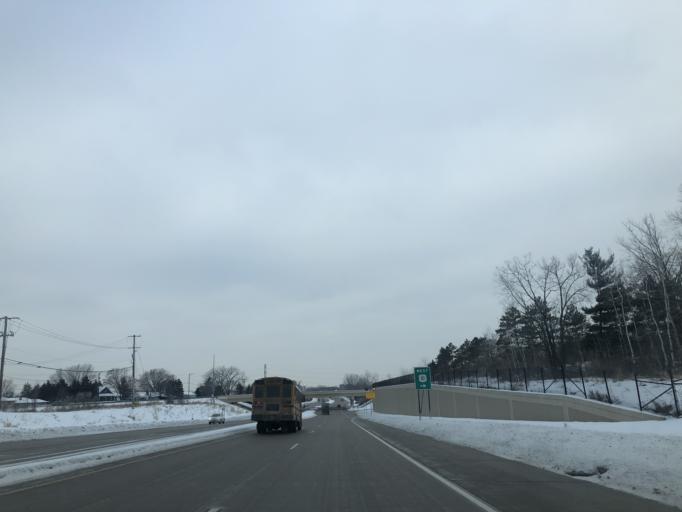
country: US
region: Minnesota
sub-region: Ramsey County
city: Shoreview
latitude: 45.0793
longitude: -93.1730
